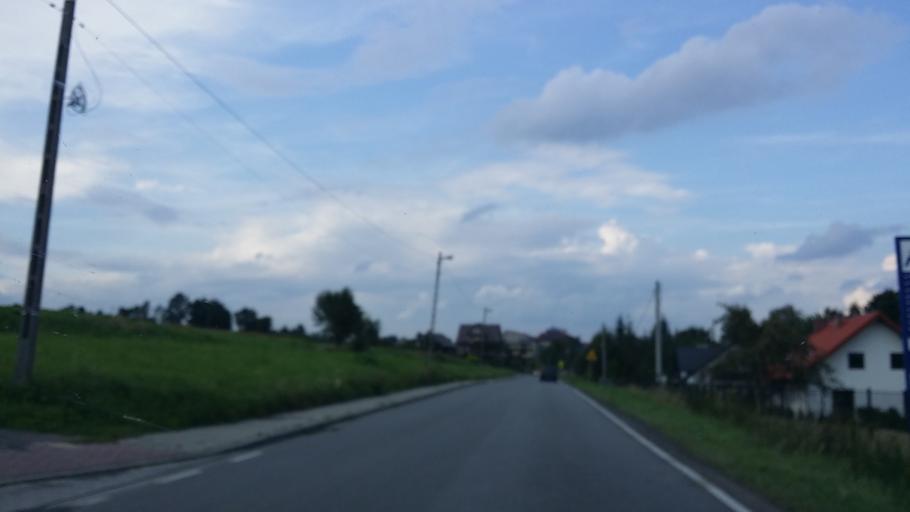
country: PL
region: Lesser Poland Voivodeship
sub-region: Powiat wielicki
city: Pawlikowice
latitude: 49.9194
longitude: 20.0287
